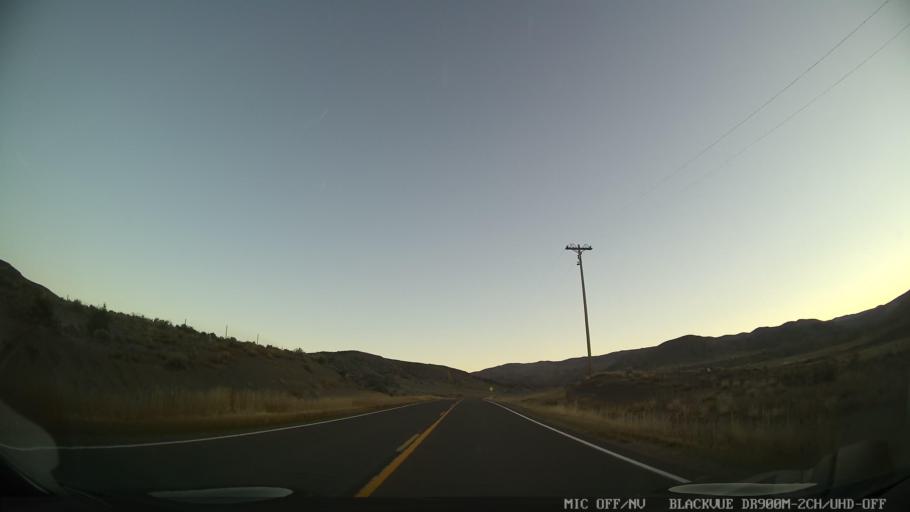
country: US
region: Colorado
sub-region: Eagle County
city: Edwards
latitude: 39.7387
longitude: -106.6787
